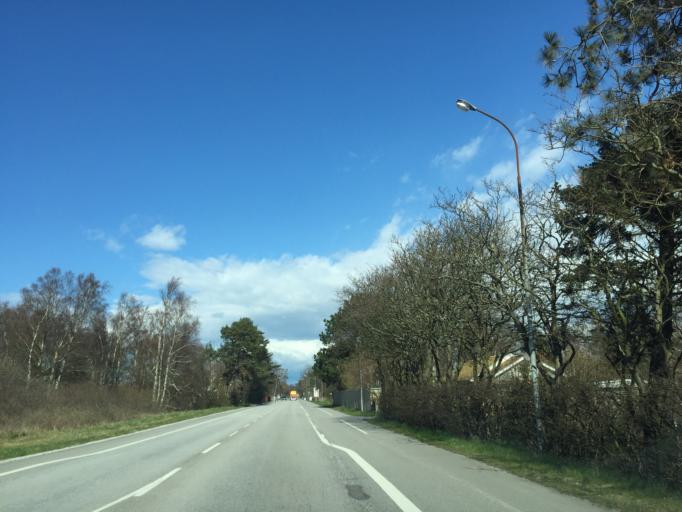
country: SE
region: Skane
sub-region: Vellinge Kommun
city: Skanor med Falsterbo
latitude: 55.4032
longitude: 12.8380
